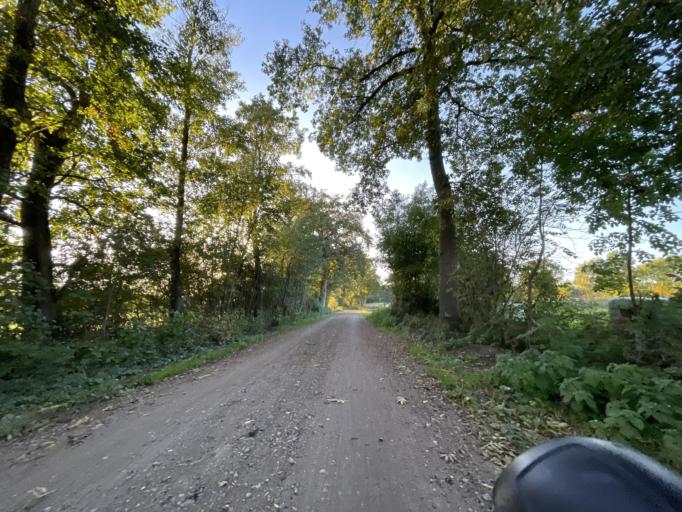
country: DE
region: Lower Saxony
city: Vastorf
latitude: 53.1993
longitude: 10.5340
